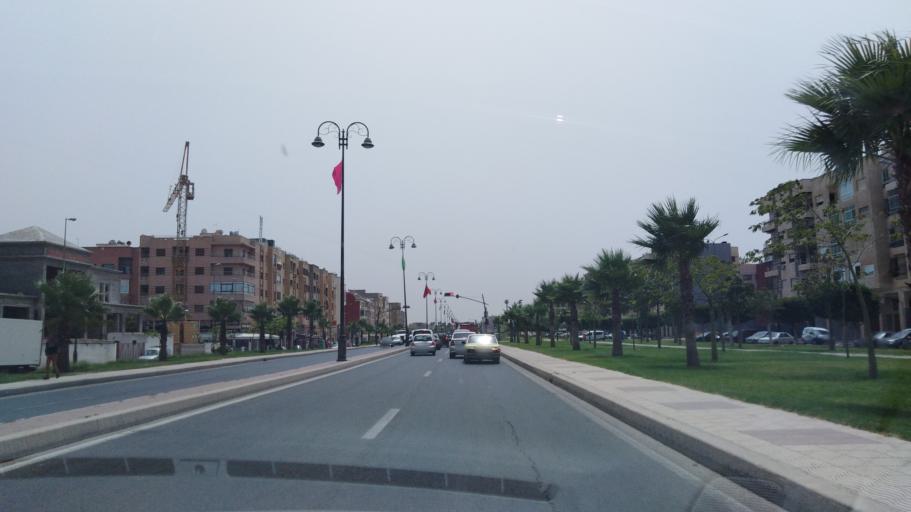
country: MA
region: Chaouia-Ouardigha
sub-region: Settat Province
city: Berrechid
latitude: 33.2767
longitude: -7.5823
